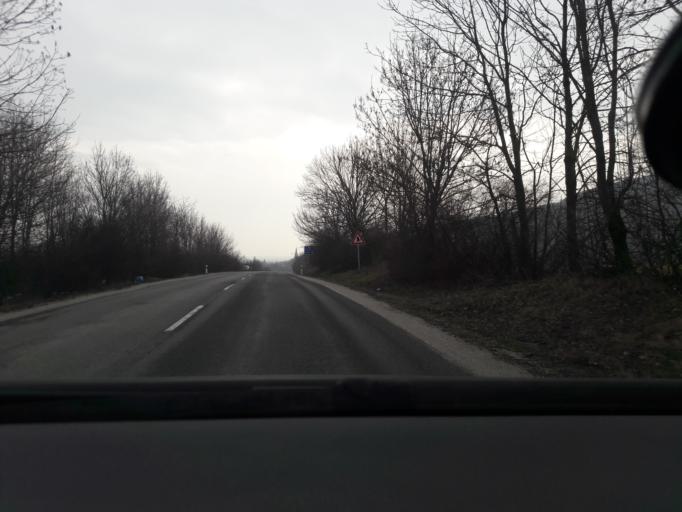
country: SK
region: Trnavsky
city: Smolenice
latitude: 48.4770
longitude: 17.4311
